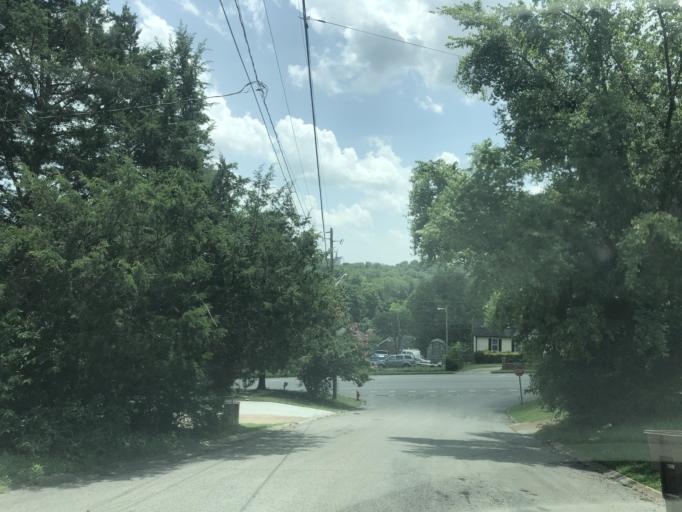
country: US
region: Tennessee
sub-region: Williamson County
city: Brentwood Estates
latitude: 36.0533
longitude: -86.6858
